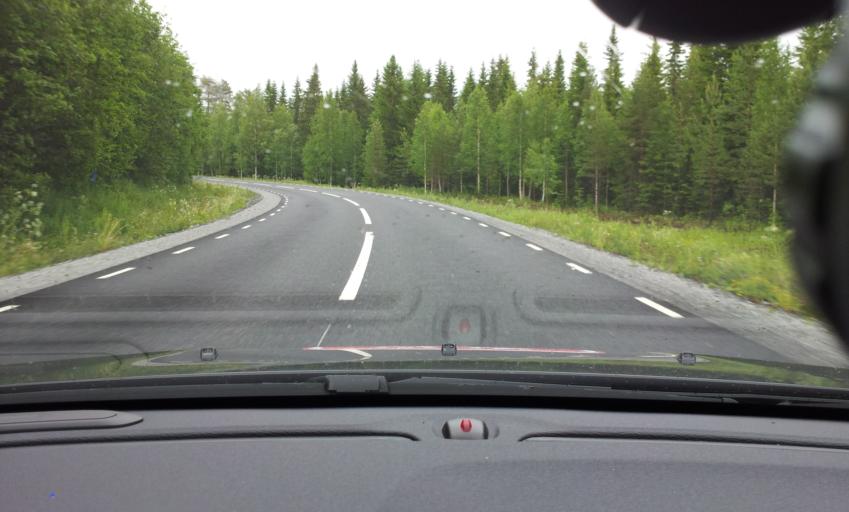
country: SE
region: Jaemtland
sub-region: OEstersunds Kommun
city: Lit
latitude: 63.7423
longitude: 14.8111
